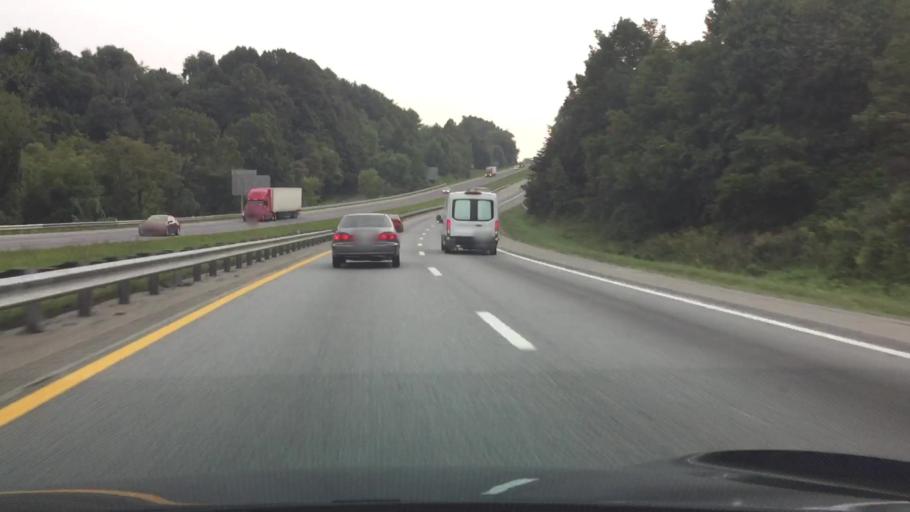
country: US
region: Virginia
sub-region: Pulaski County
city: Pulaski
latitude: 37.0152
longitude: -80.7412
